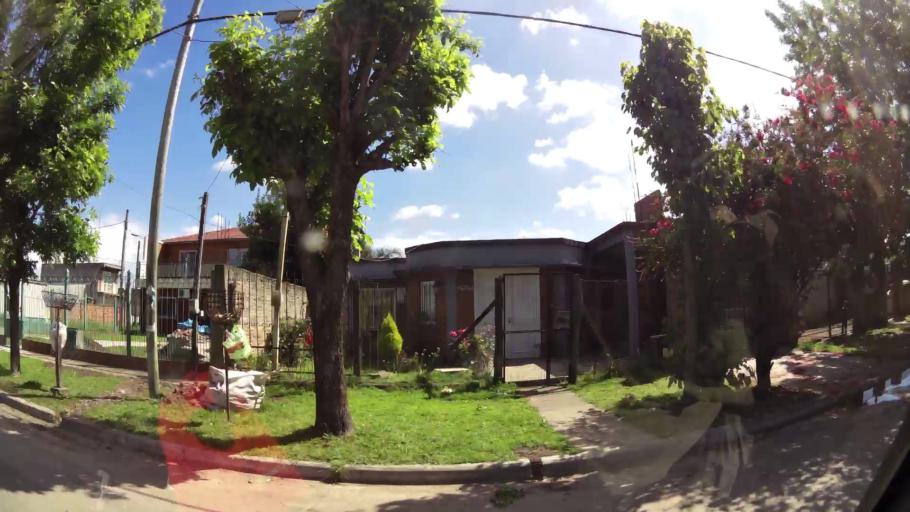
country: AR
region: Buenos Aires
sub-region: Partido de Quilmes
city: Quilmes
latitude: -34.8227
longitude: -58.2618
